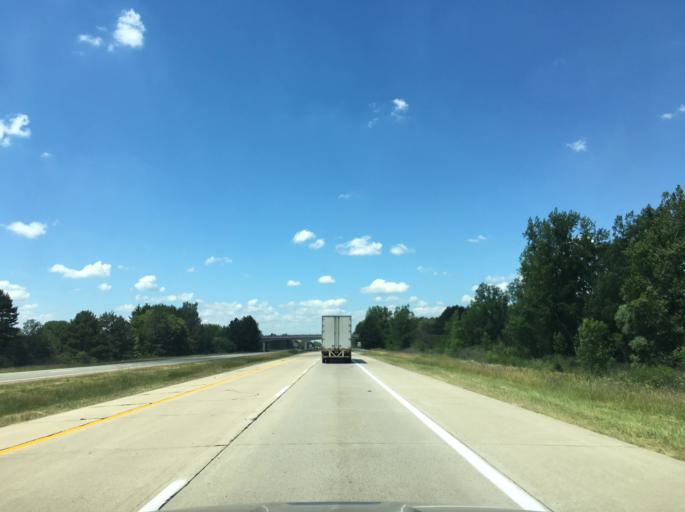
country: US
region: Michigan
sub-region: Bay County
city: Auburn
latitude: 43.5973
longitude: -84.1058
